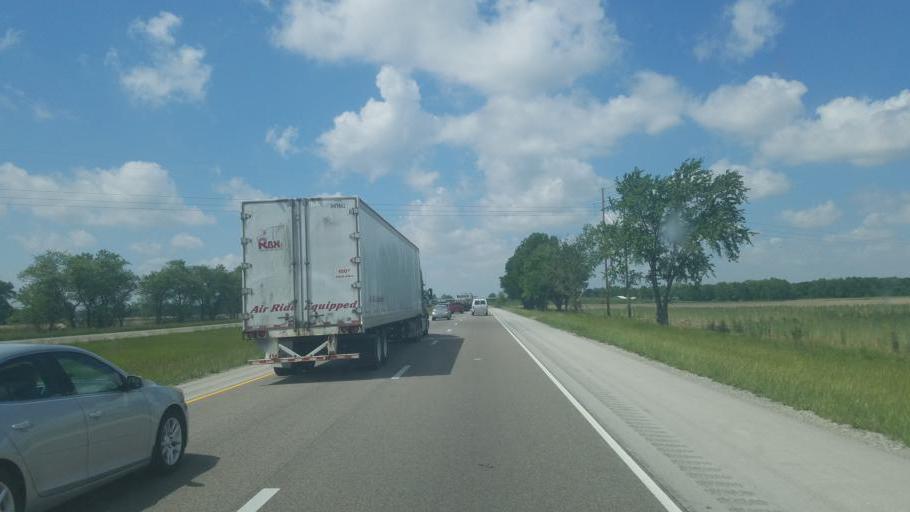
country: US
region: Illinois
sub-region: Cumberland County
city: Toledo
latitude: 39.2316
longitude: -88.2134
